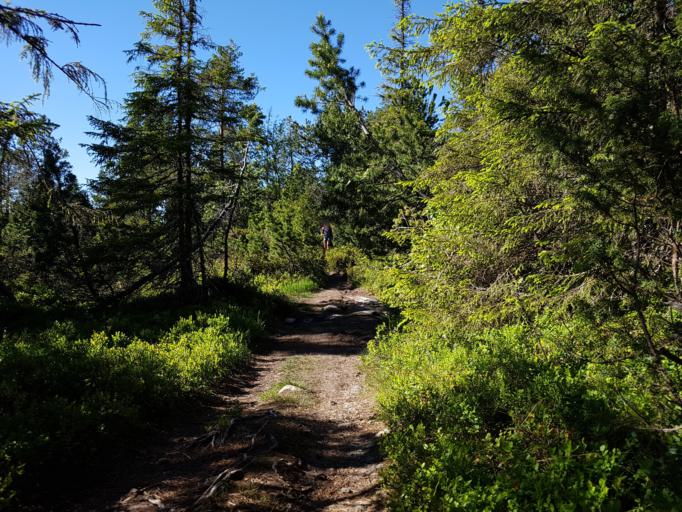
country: NO
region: Sor-Trondelag
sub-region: Trondheim
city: Trondheim
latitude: 63.4114
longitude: 10.3097
